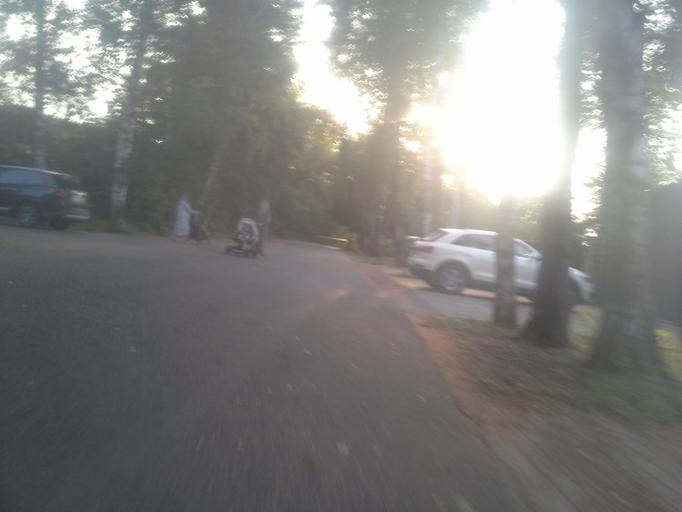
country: RU
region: Moskovskaya
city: Nikolina Gora
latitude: 55.7292
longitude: 37.0971
